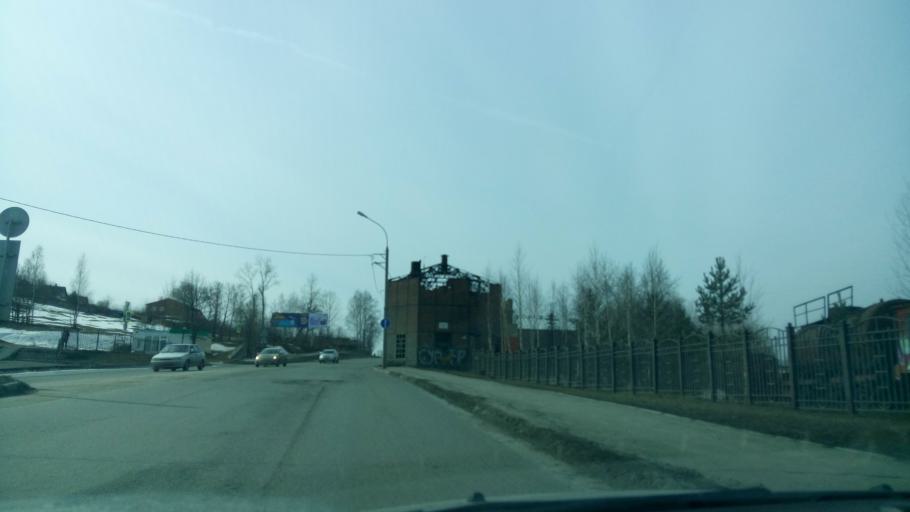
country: RU
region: Sverdlovsk
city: Nizhniy Tagil
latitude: 57.9032
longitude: 59.9474
